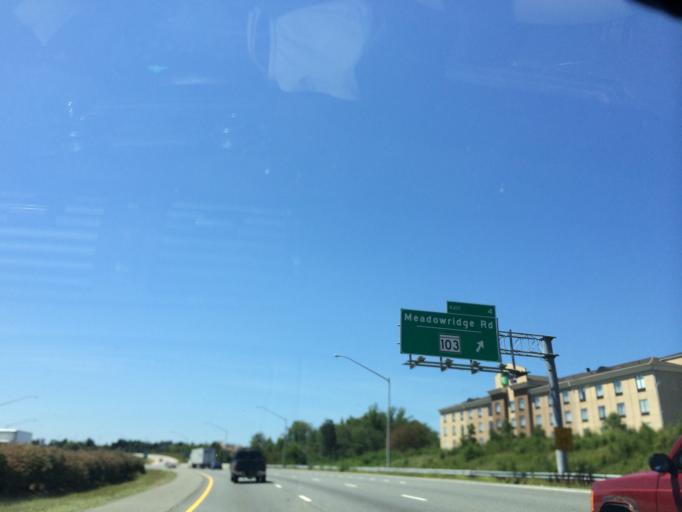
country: US
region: Maryland
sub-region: Howard County
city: Ilchester
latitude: 39.2070
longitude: -76.7779
